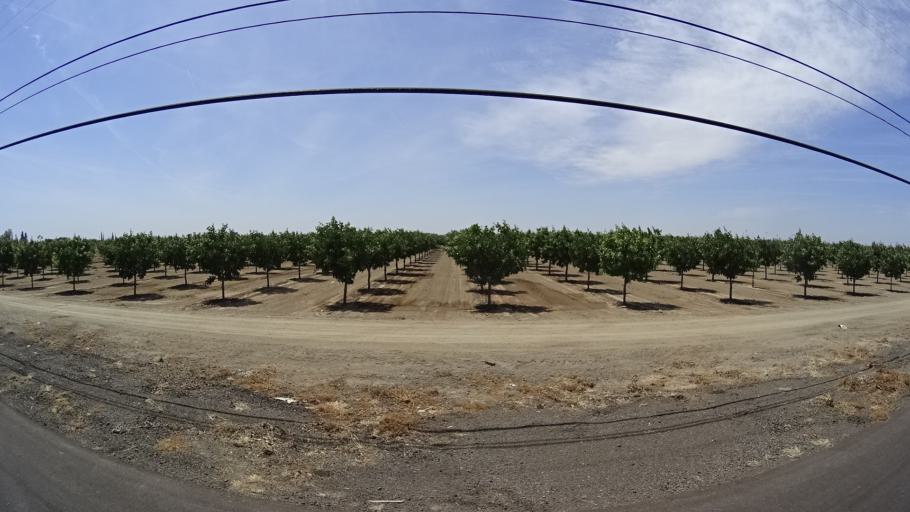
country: US
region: California
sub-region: Kings County
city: Hanford
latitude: 36.3426
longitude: -119.6780
